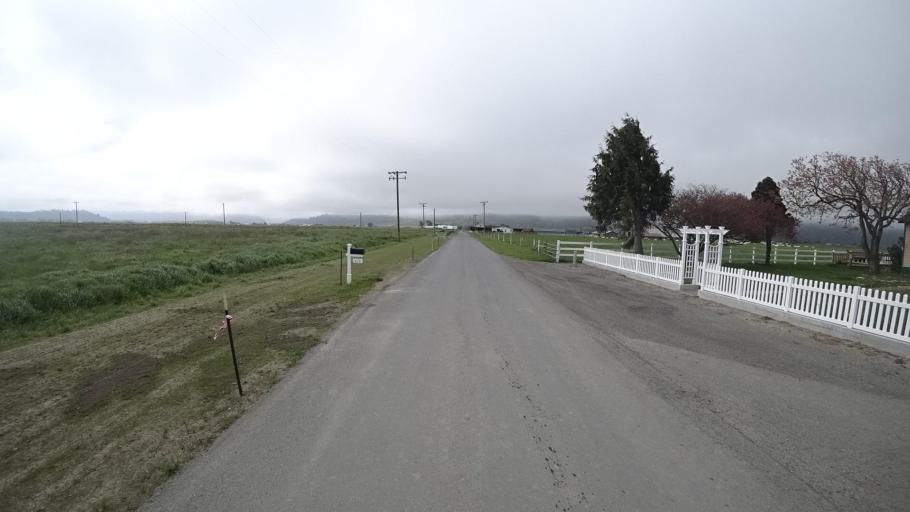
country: US
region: California
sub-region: Humboldt County
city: Fortuna
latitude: 40.5786
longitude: -124.1878
